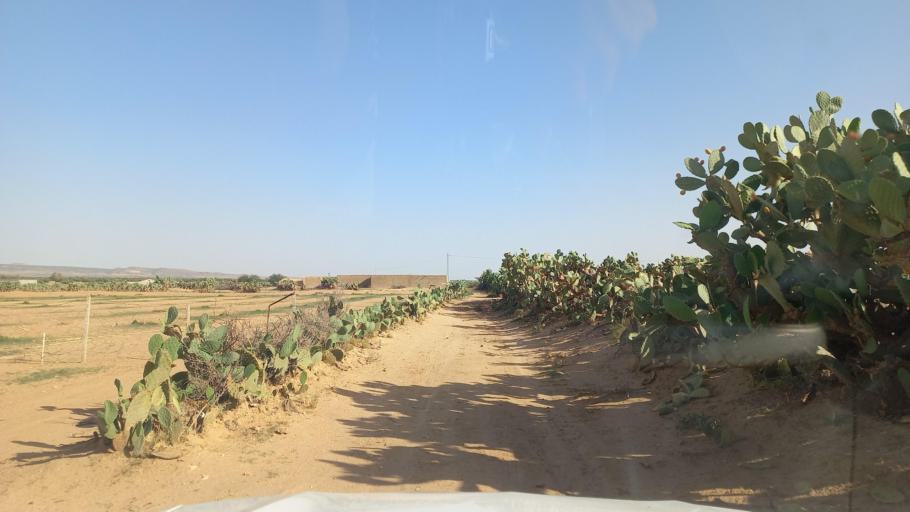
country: TN
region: Al Qasrayn
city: Sbiba
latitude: 35.3217
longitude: 9.0241
